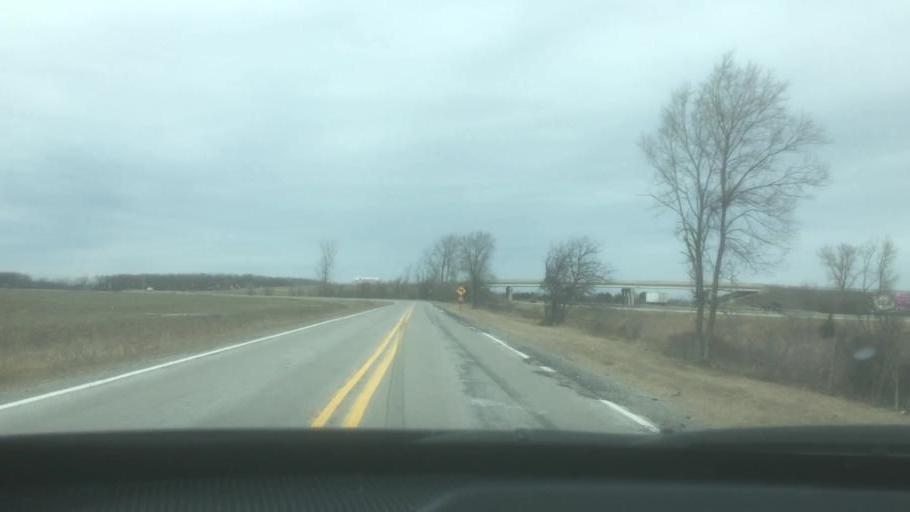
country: US
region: Michigan
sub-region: Bay County
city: Bay City
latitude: 43.6219
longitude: -83.9533
